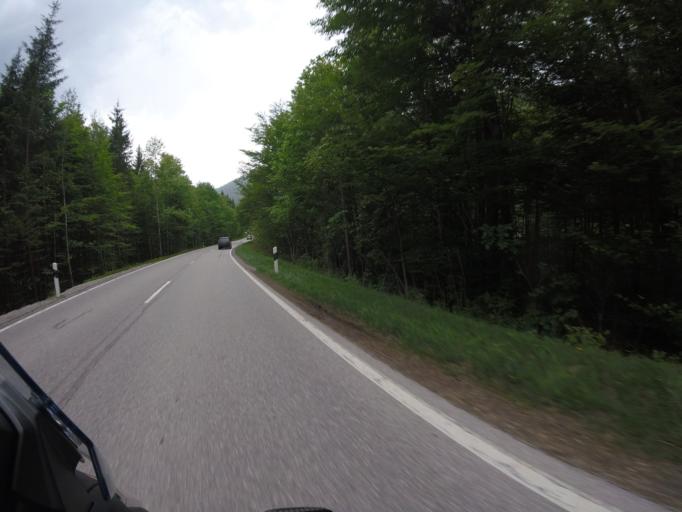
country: DE
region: Bavaria
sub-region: Upper Bavaria
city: Lenggries
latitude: 47.6008
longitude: 11.5705
